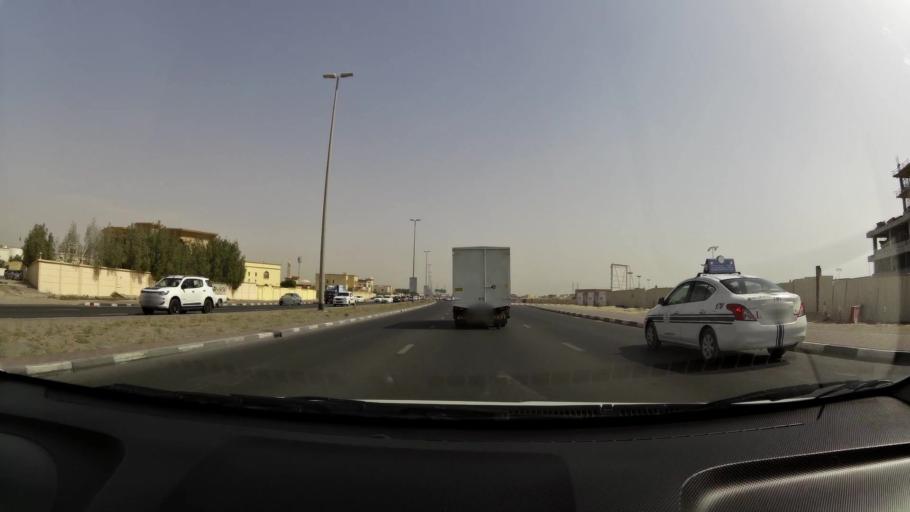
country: AE
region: Ash Shariqah
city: Sharjah
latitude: 25.2777
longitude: 55.3961
